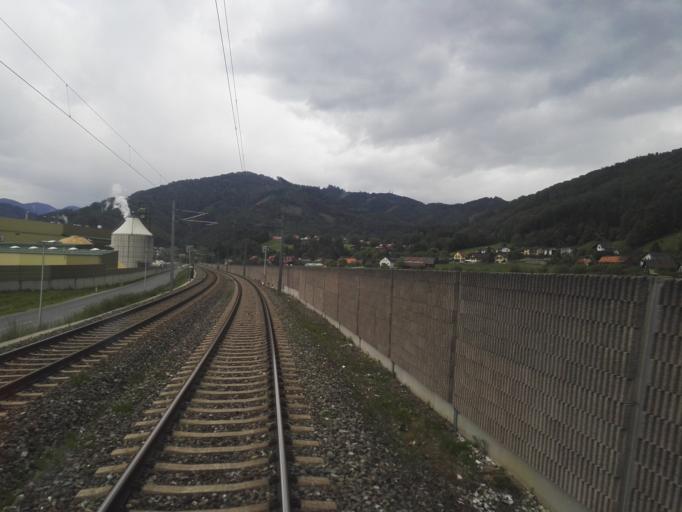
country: AT
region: Styria
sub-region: Politischer Bezirk Graz-Umgebung
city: Frohnleiten
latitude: 47.2801
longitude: 15.3285
